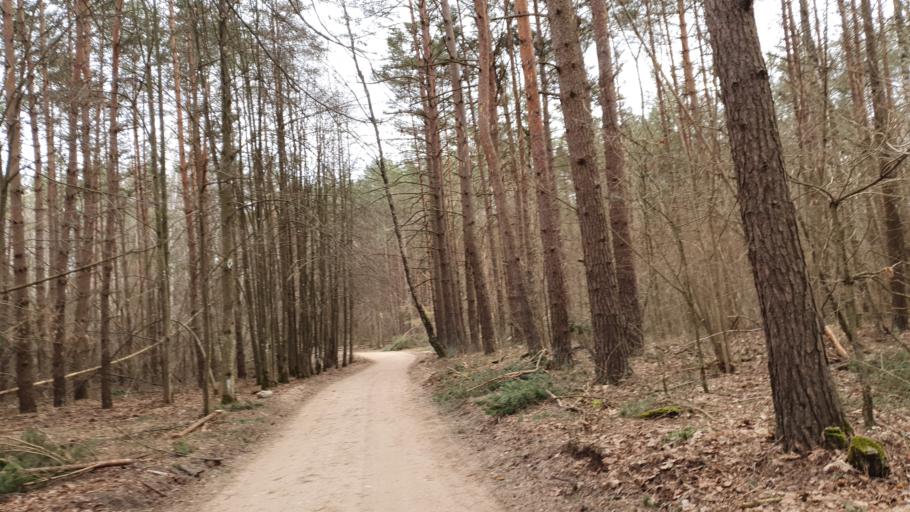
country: LT
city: Grigiskes
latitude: 54.7322
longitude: 25.0279
